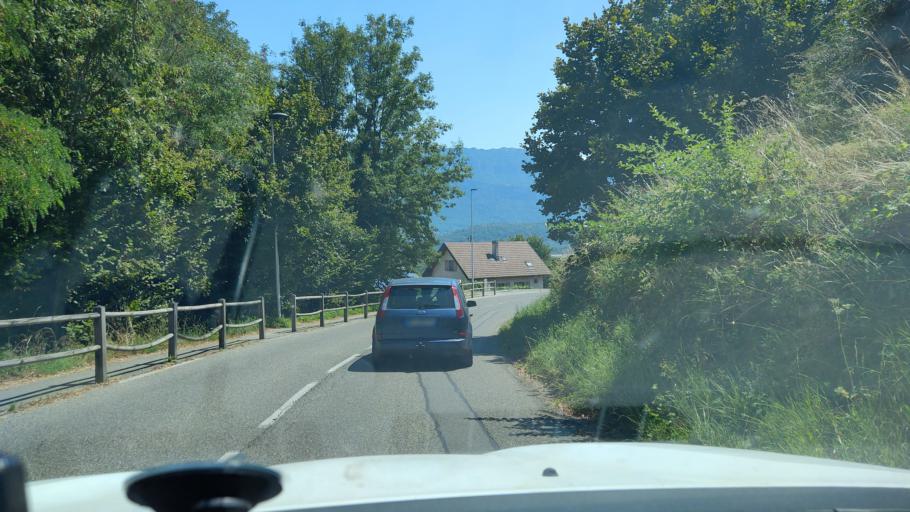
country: FR
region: Rhone-Alpes
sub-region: Departement de la Savoie
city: Le Bourget-du-Lac
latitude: 45.6518
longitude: 5.8535
